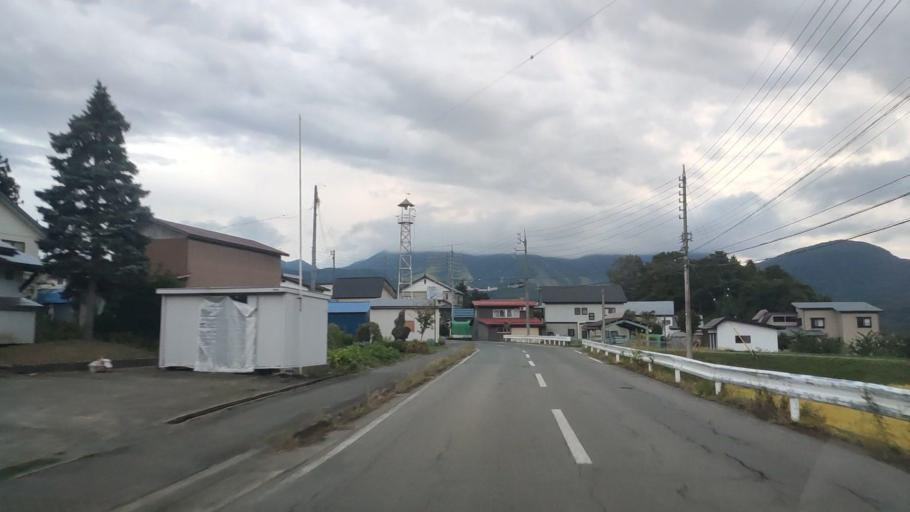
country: JP
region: Nagano
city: Iiyama
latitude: 36.8560
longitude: 138.4089
